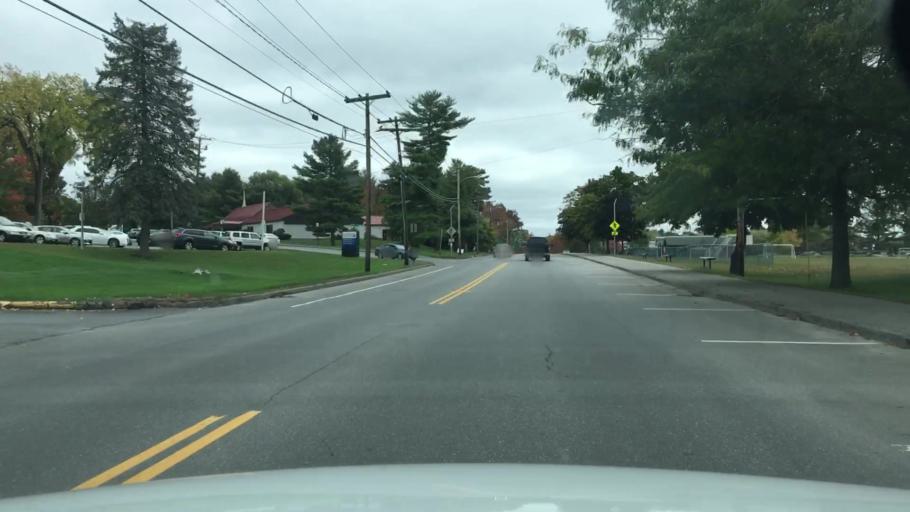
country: US
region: Maine
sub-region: Kennebec County
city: Waterville
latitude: 44.5644
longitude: -69.6474
